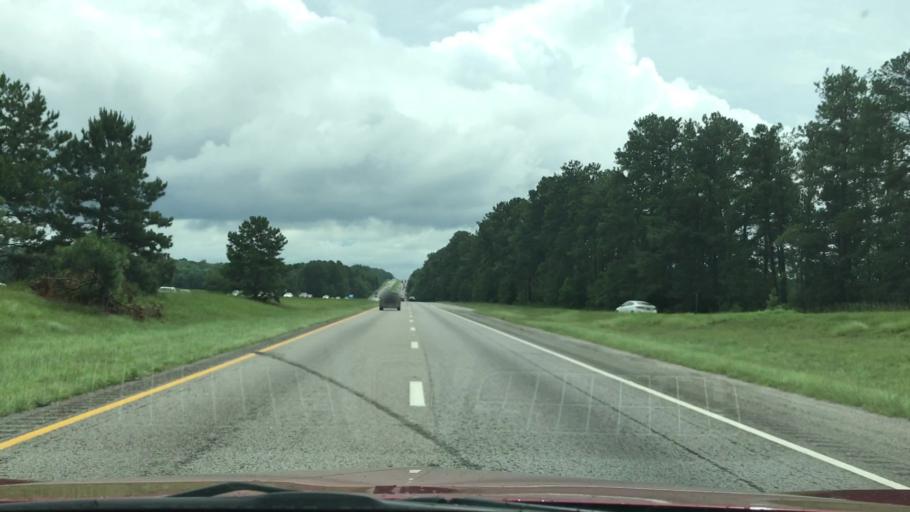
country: US
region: South Carolina
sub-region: Calhoun County
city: Saint Matthews
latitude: 33.6328
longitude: -80.8752
